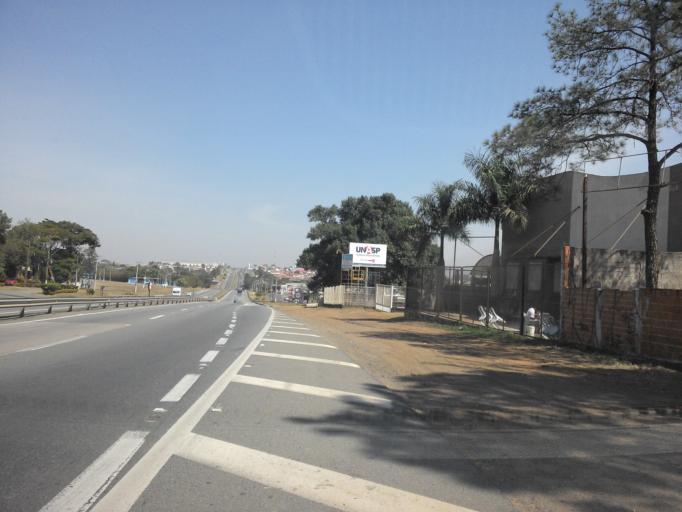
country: BR
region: Sao Paulo
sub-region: Hortolandia
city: Hortolandia
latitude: -22.9027
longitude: -47.2279
